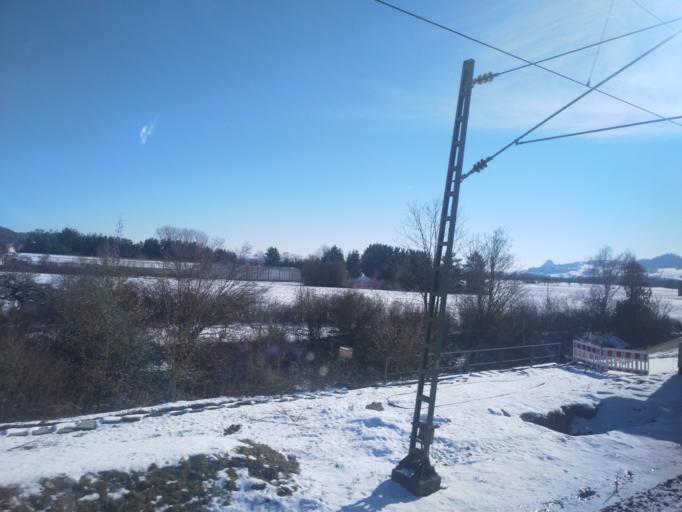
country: DE
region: Baden-Wuerttemberg
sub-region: Freiburg Region
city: Neuhausen
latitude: 47.8349
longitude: 8.7687
